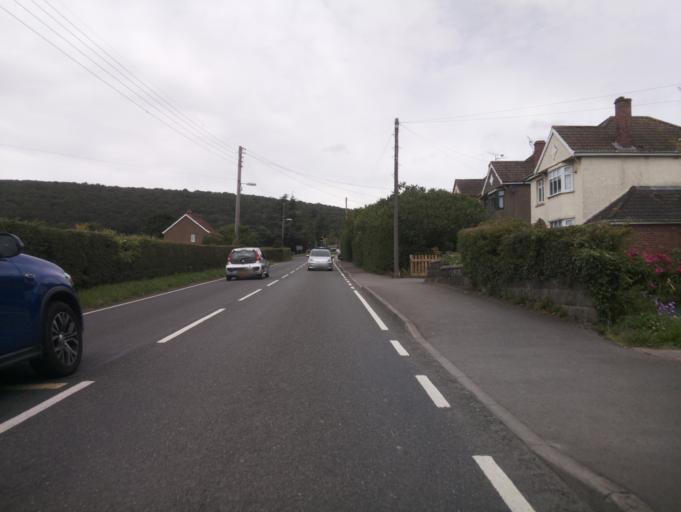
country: GB
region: England
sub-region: Somerset
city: Cheddar
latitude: 51.2864
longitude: -2.7901
